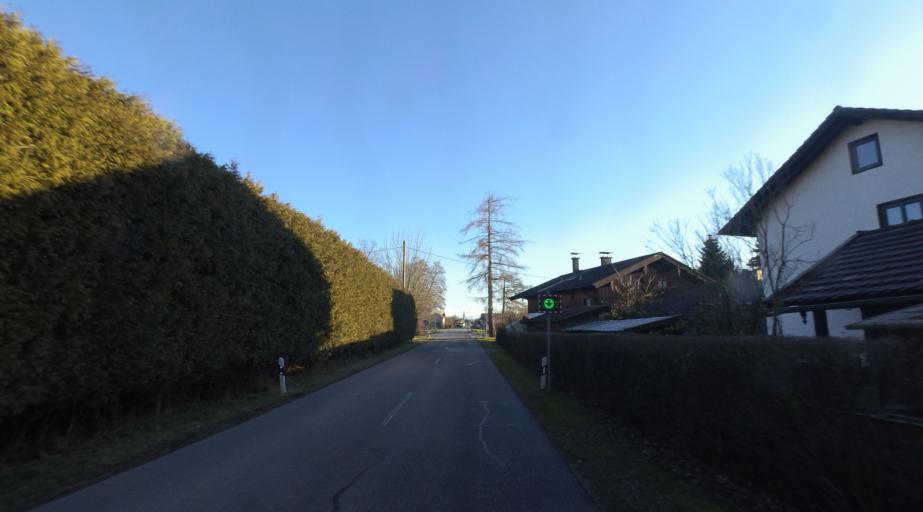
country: DE
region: Bavaria
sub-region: Upper Bavaria
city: Kirchanschoring
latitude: 47.9611
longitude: 12.8266
